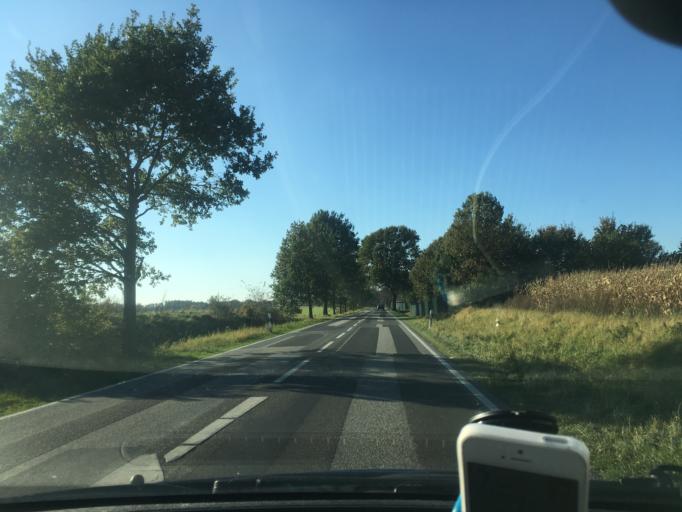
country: DE
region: Mecklenburg-Vorpommern
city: Zarrentin
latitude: 53.5302
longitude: 10.9626
